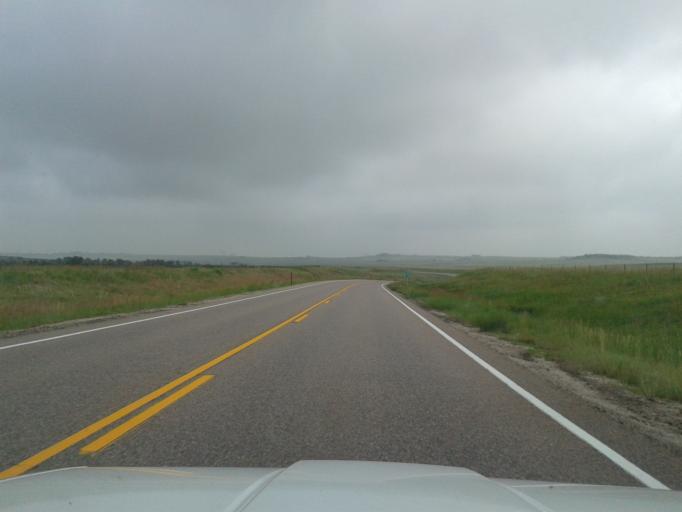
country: US
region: Colorado
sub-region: El Paso County
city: Woodmoor
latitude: 39.2147
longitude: -104.7084
